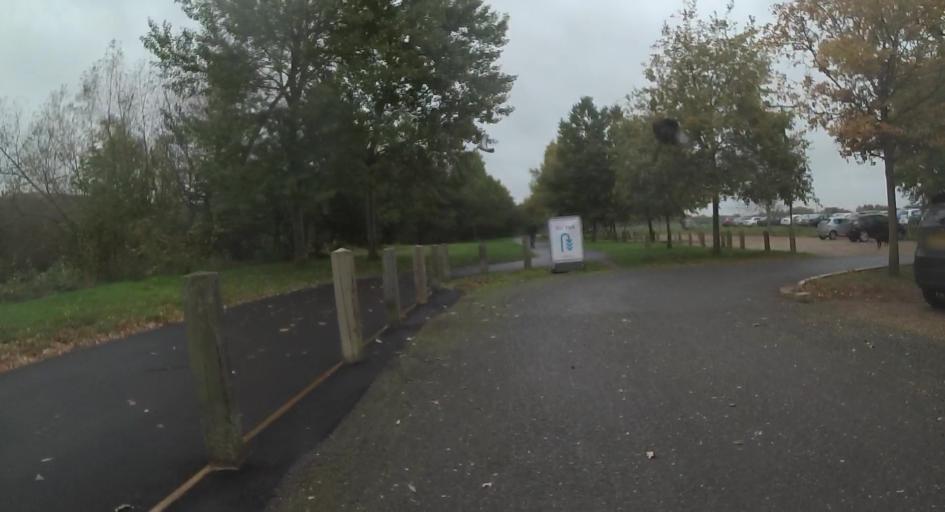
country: GB
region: England
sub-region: Surrey
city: Byfleet
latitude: 51.3525
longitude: -0.4662
